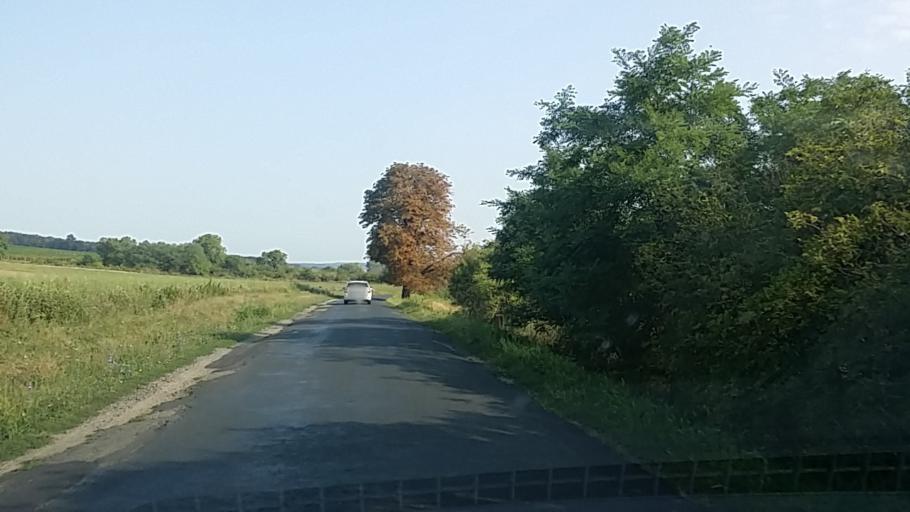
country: HU
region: Gyor-Moson-Sopron
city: Fertorakos
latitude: 47.6910
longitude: 16.6631
